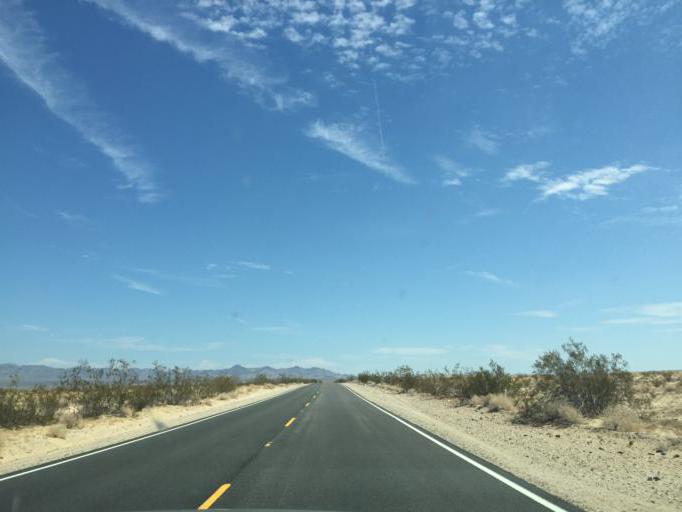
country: US
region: California
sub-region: Riverside County
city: Mesa Verde
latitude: 34.0965
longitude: -115.0322
